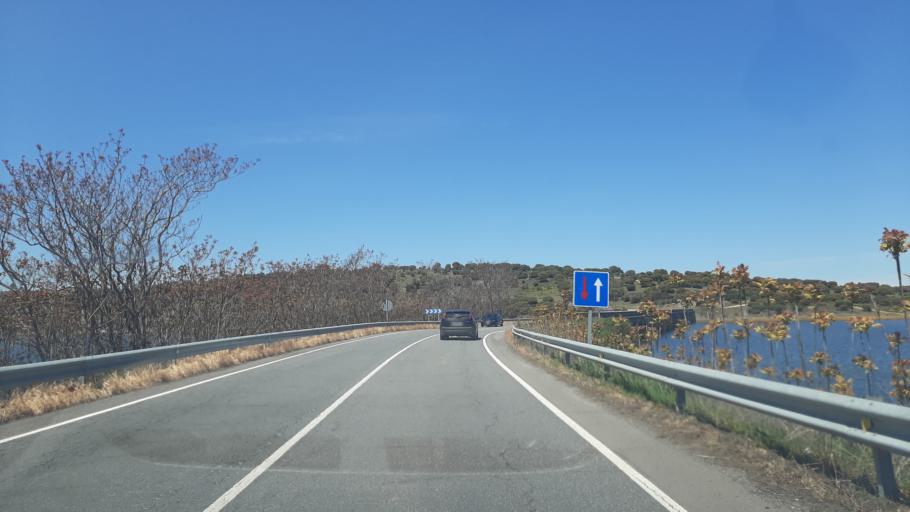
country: ES
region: Castille and Leon
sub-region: Provincia de Salamanca
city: Guijo de Avila
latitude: 40.5514
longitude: -5.6272
